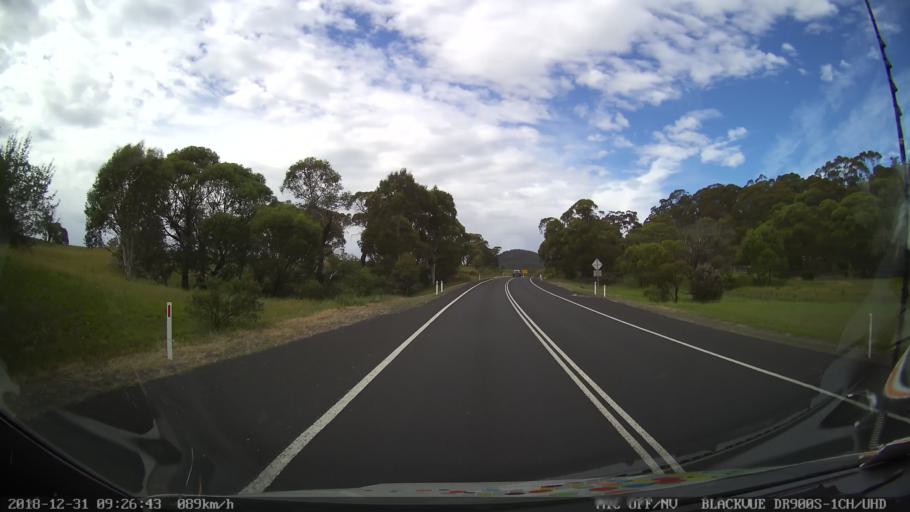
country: AU
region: New South Wales
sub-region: Snowy River
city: Jindabyne
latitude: -36.4514
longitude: 148.4937
